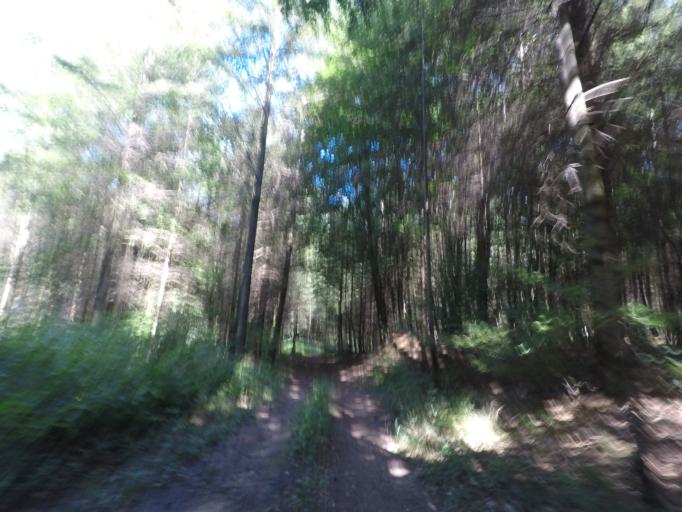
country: LU
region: Luxembourg
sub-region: Canton de Capellen
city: Kopstal
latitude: 49.6471
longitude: 6.0664
